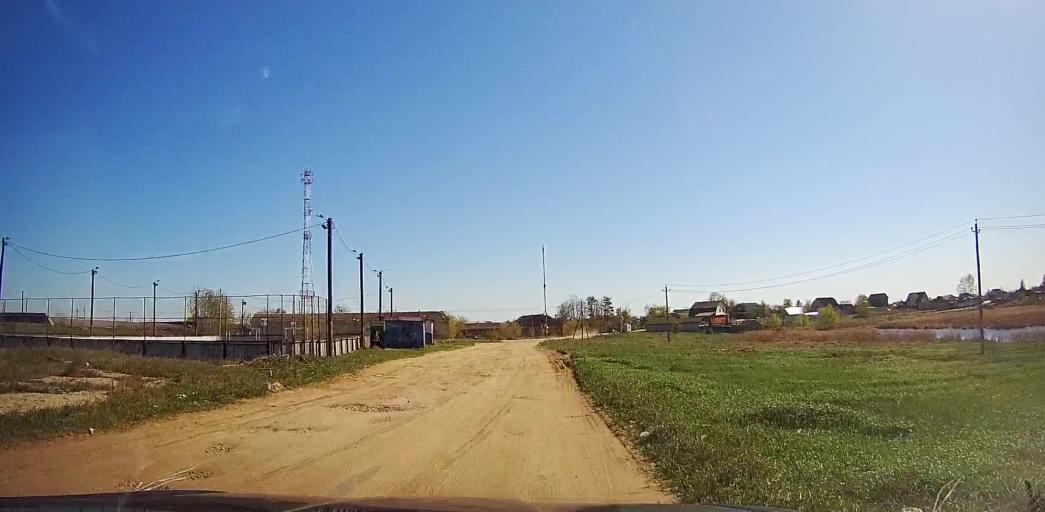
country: RU
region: Moskovskaya
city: Ramenskoye
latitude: 55.5551
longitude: 38.2864
